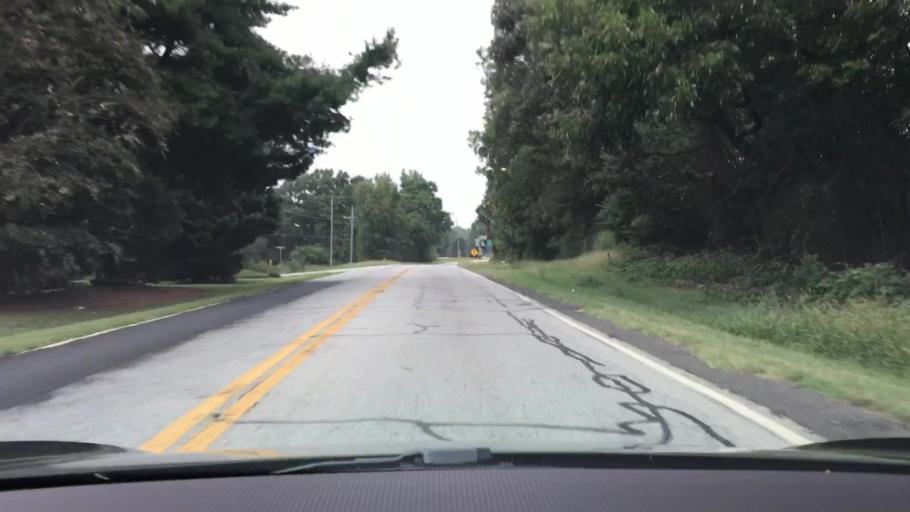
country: US
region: Georgia
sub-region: Barrow County
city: Russell
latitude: 33.9706
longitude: -83.6865
